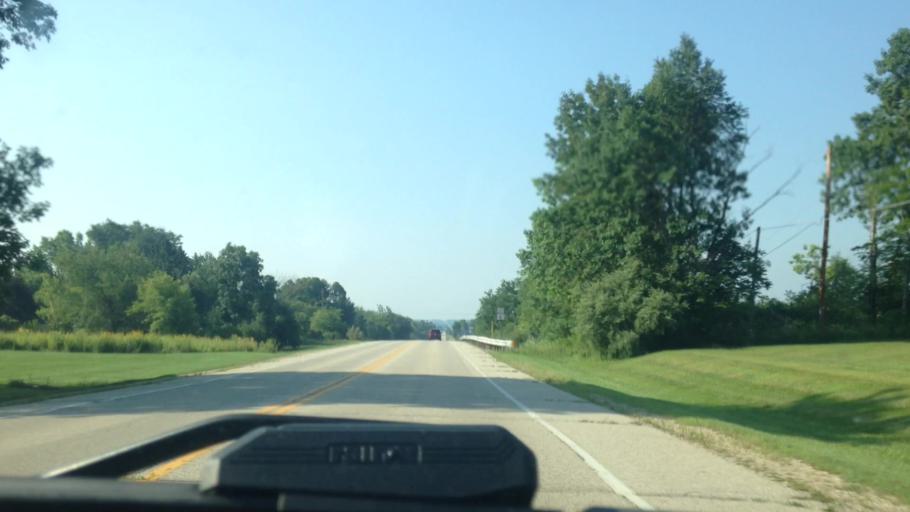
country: US
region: Wisconsin
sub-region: Washington County
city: Slinger
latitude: 43.2997
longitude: -88.2608
